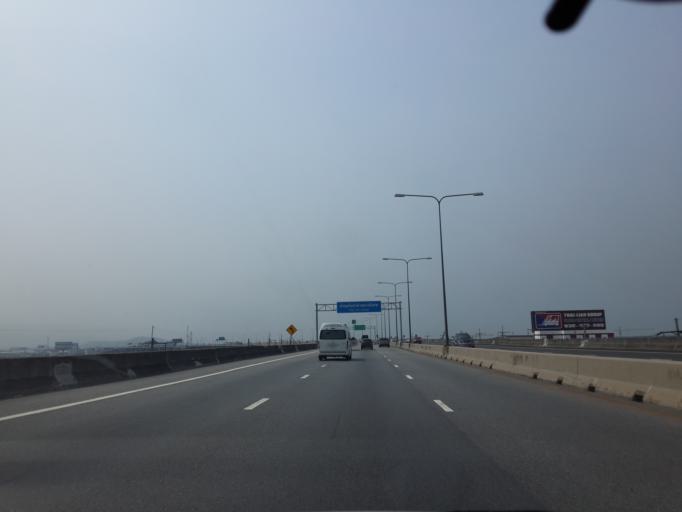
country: TH
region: Chachoengsao
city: Bang Pakong
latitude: 13.4682
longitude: 100.9971
